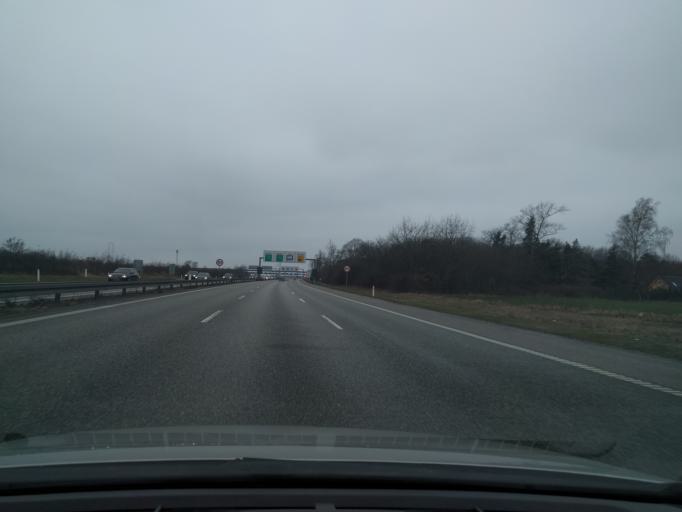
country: DK
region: Zealand
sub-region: Slagelse Kommune
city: Korsor
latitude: 55.3459
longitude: 11.1169
